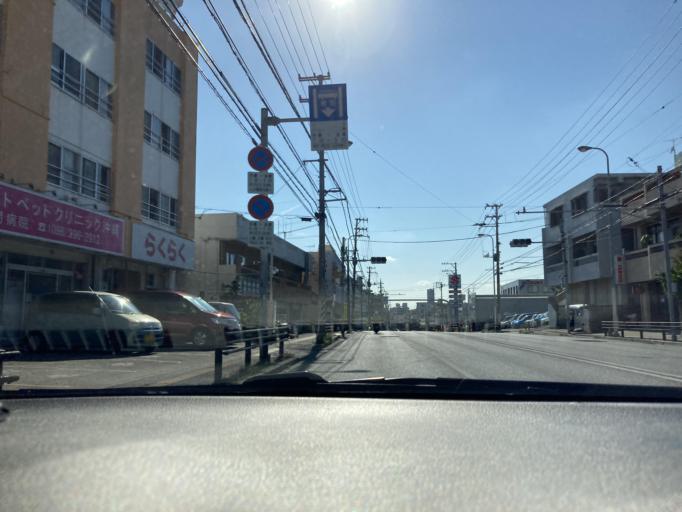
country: JP
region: Okinawa
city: Tomigusuku
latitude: 26.1979
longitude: 127.7103
